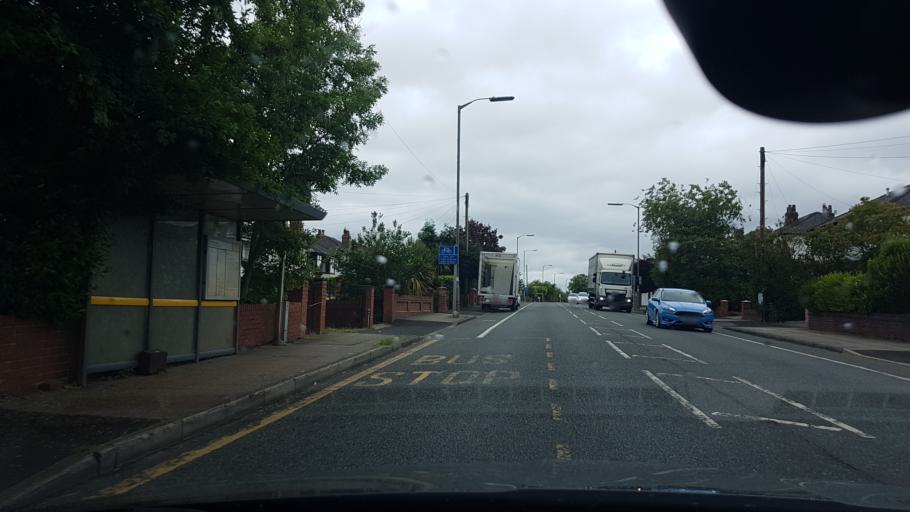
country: GB
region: England
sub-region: Borough of Bury
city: Radcliffe
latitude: 53.5862
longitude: -2.3249
